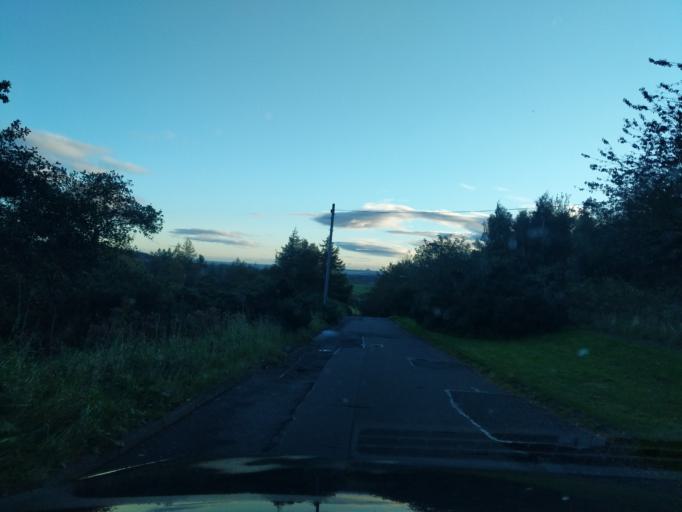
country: GB
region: Scotland
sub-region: Midlothian
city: Loanhead
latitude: 55.8890
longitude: -3.2079
